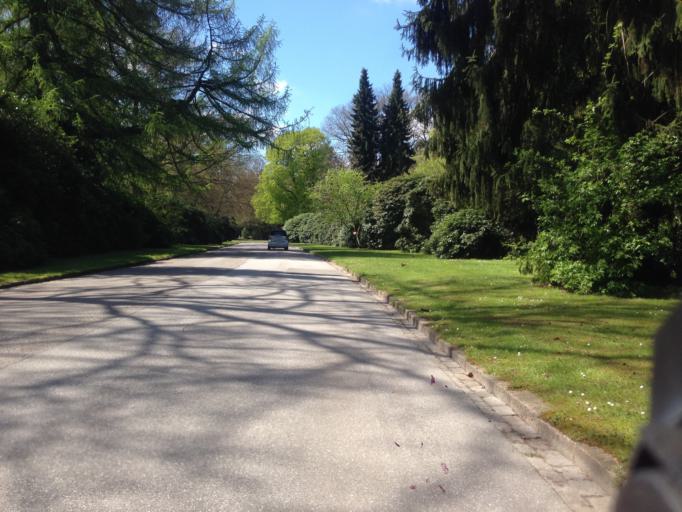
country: DE
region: Hamburg
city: Ohlsdorf
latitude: 53.6252
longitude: 10.0448
